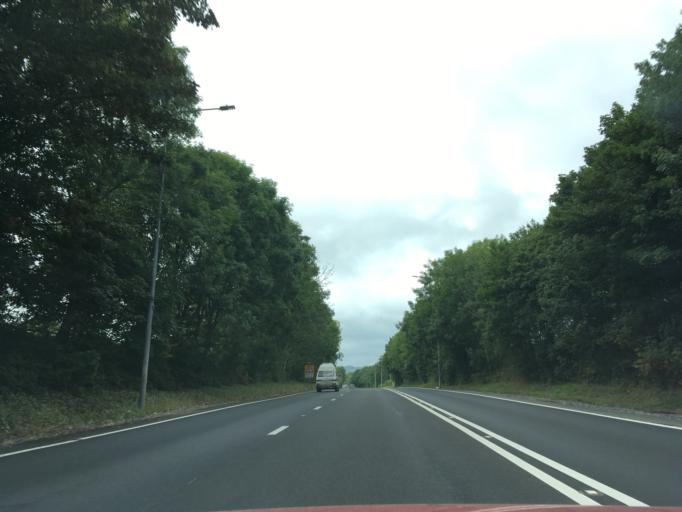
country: GB
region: Wales
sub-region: Carmarthenshire
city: Saint Clears
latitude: 51.8193
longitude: -4.5132
